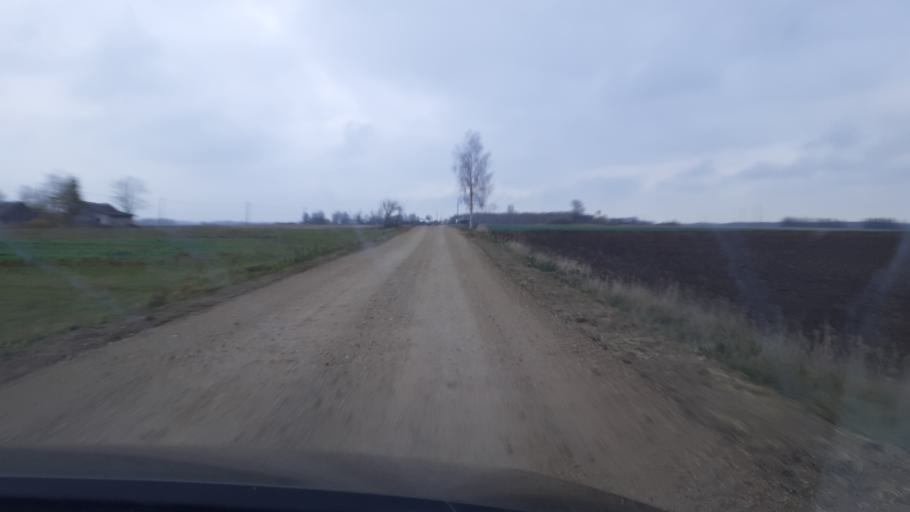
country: LV
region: Talsu Rajons
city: Sabile
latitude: 56.9354
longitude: 22.4179
